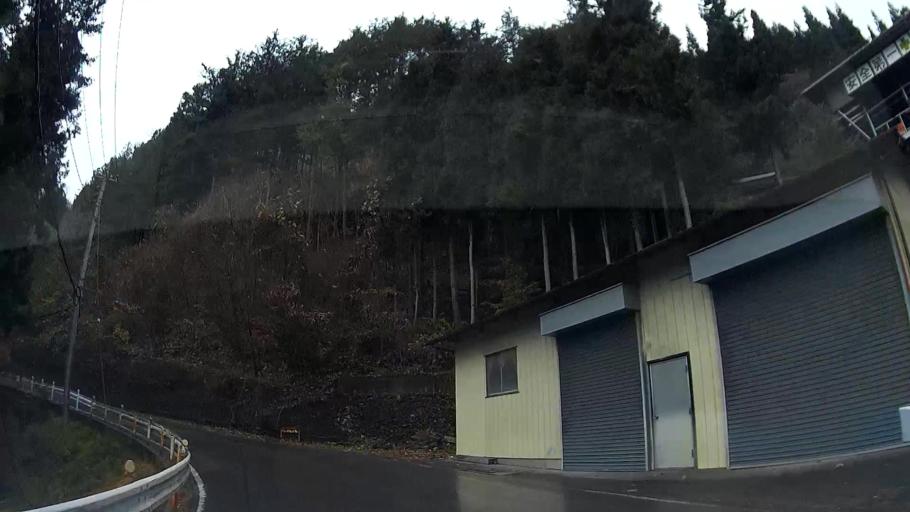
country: JP
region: Saitama
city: Chichibu
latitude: 35.9469
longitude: 138.9113
